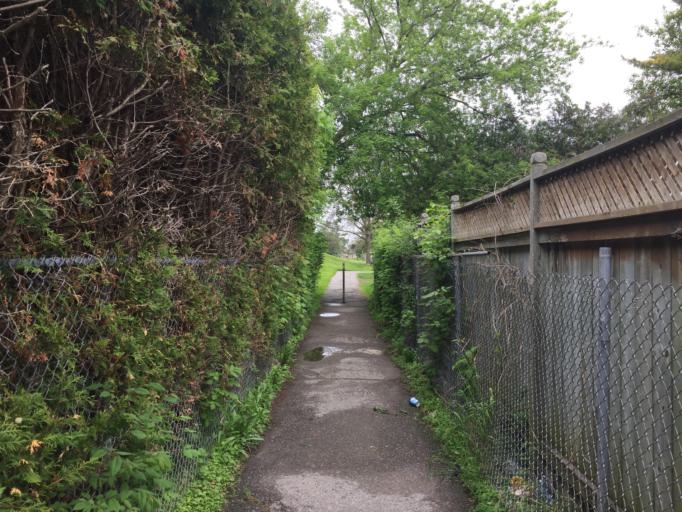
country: CA
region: Ontario
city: Oshawa
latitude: 43.8961
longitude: -78.8782
